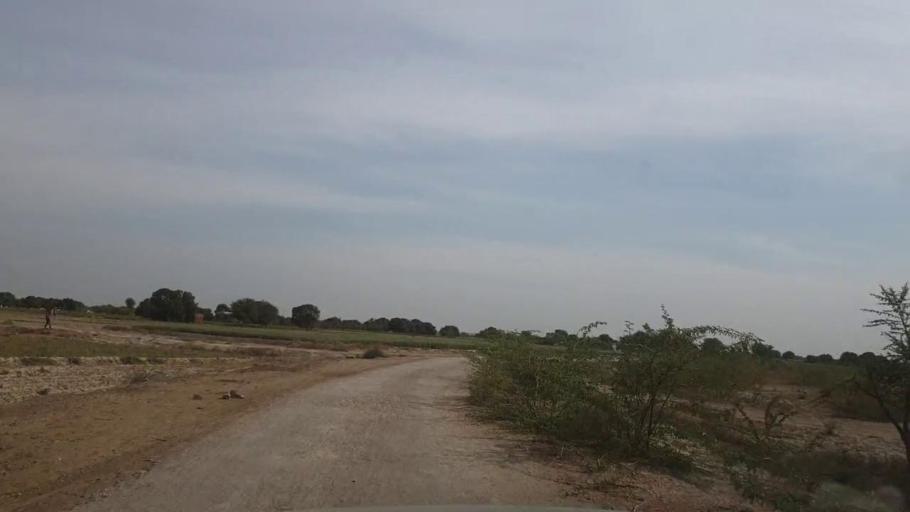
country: PK
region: Sindh
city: Nabisar
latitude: 25.0354
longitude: 69.5623
